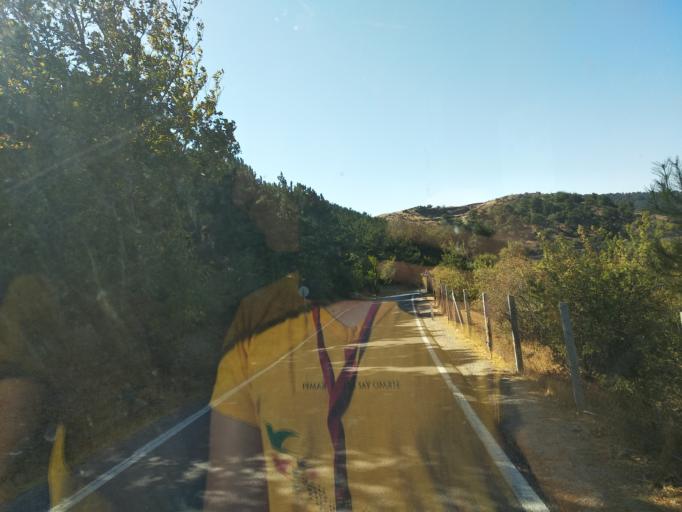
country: TR
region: Izmir
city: Gaziemir
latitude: 38.3200
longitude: 27.0094
